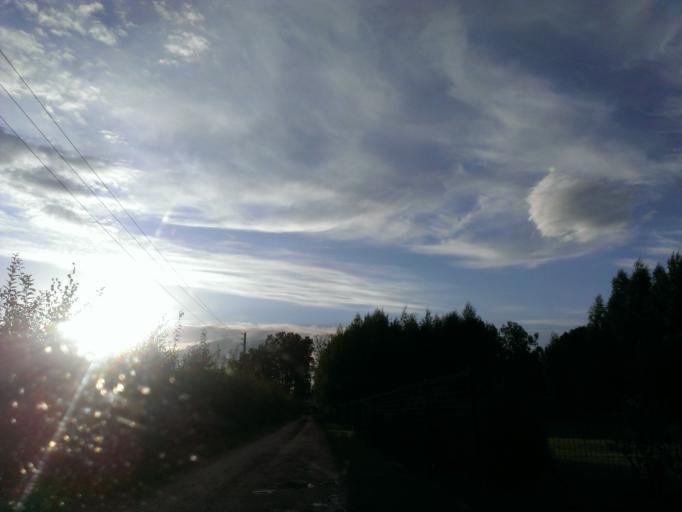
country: LV
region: Ikskile
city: Ikskile
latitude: 56.8354
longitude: 24.5216
